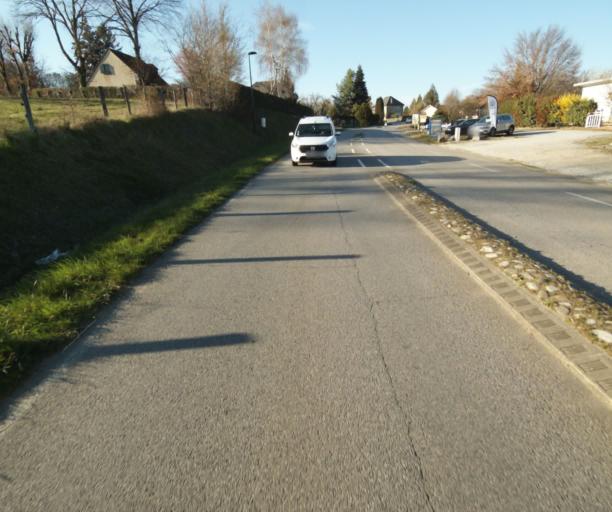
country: FR
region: Limousin
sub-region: Departement de la Correze
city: Chamboulive
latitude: 45.4248
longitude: 1.7104
